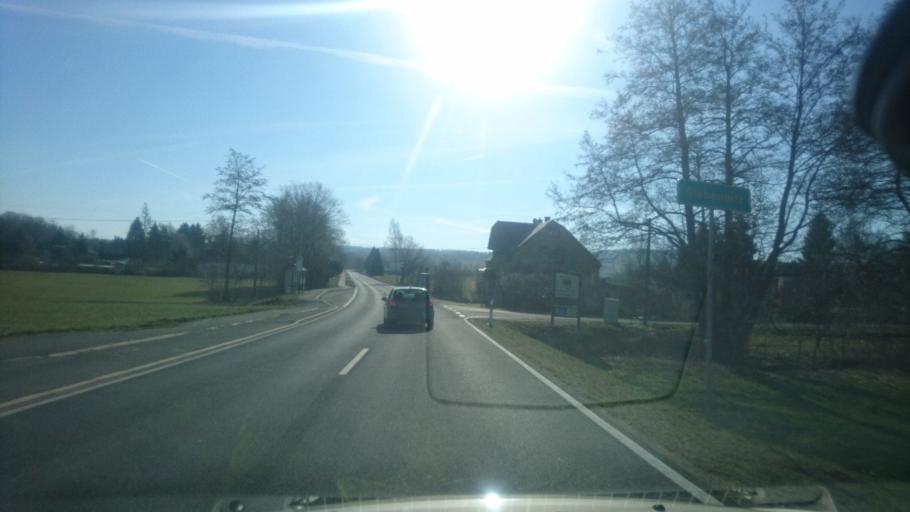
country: DE
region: Saxony
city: Neustadt Vogtland
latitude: 50.4752
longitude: 12.3343
